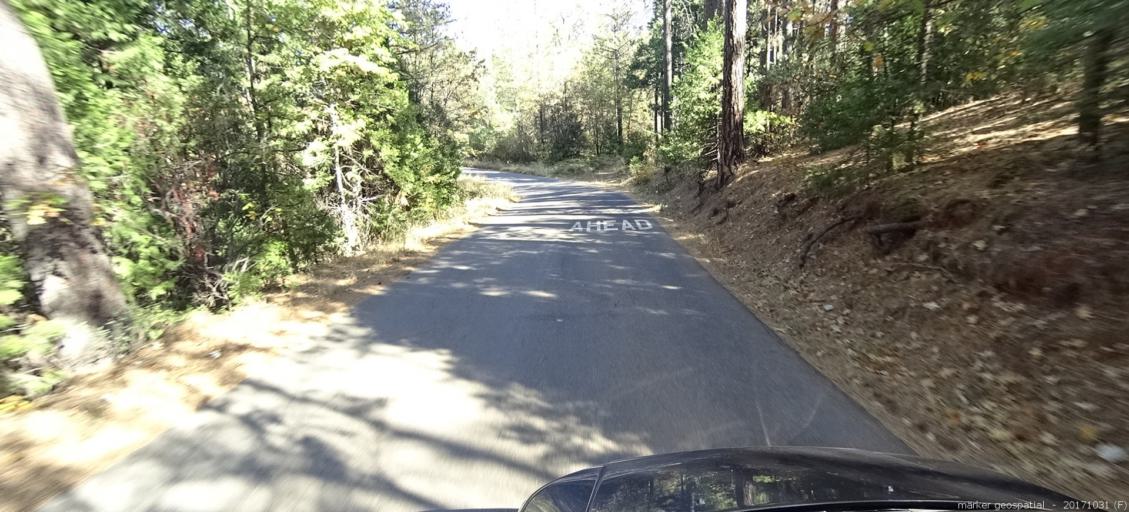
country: US
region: California
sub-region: Shasta County
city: Shingletown
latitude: 40.5113
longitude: -121.9368
